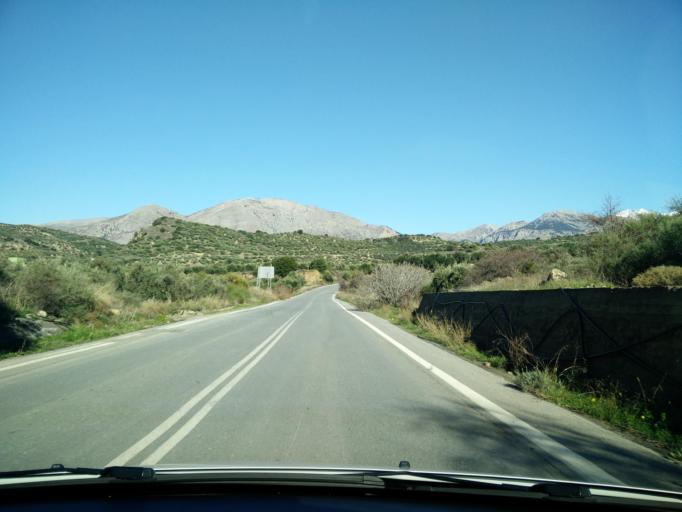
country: GR
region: Crete
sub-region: Nomos Irakleiou
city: Arkalochori
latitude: 35.0769
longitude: 25.3488
